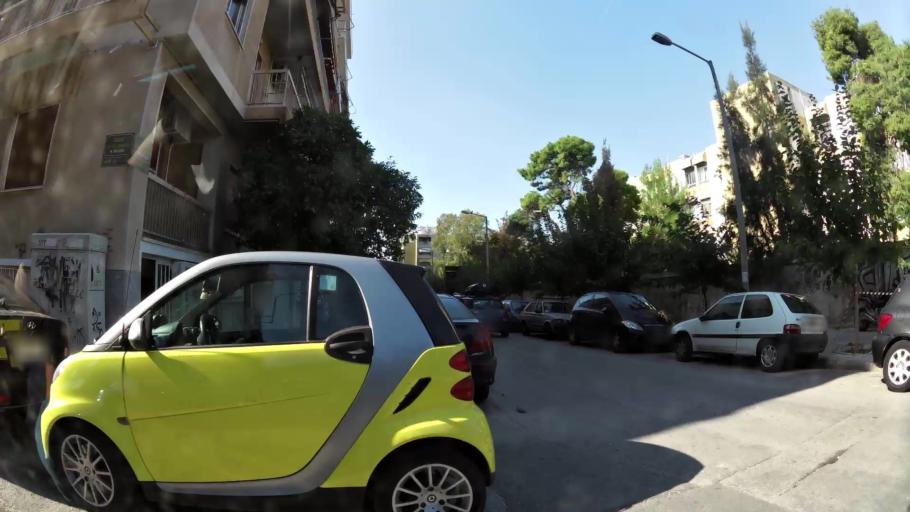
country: GR
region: Attica
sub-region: Nomarchia Athinas
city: Kaisariani
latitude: 37.9838
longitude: 23.7694
